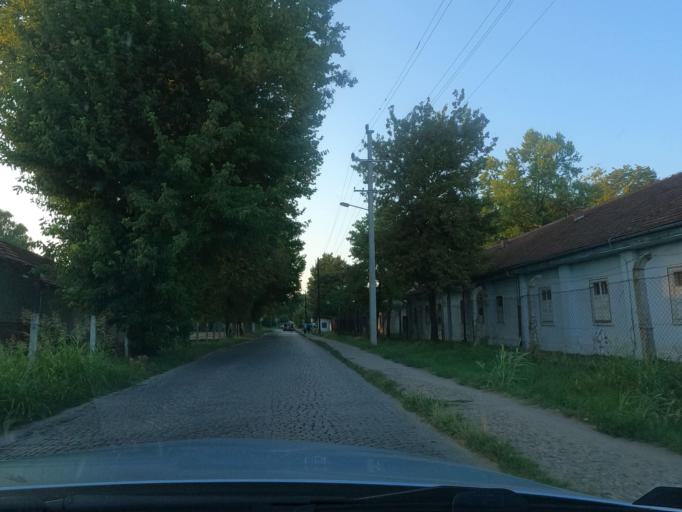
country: RS
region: Autonomna Pokrajina Vojvodina
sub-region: Juznobacki Okrug
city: Novi Sad
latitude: 45.2337
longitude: 19.8265
